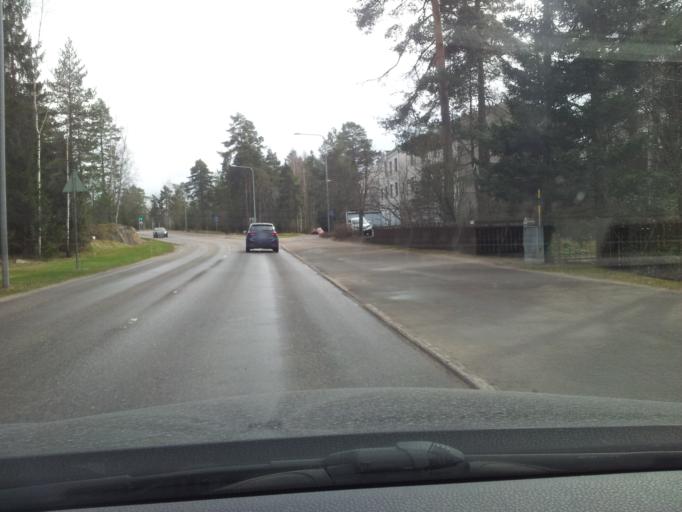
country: FI
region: Uusimaa
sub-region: Helsinki
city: Koukkuniemi
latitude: 60.1769
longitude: 24.7420
